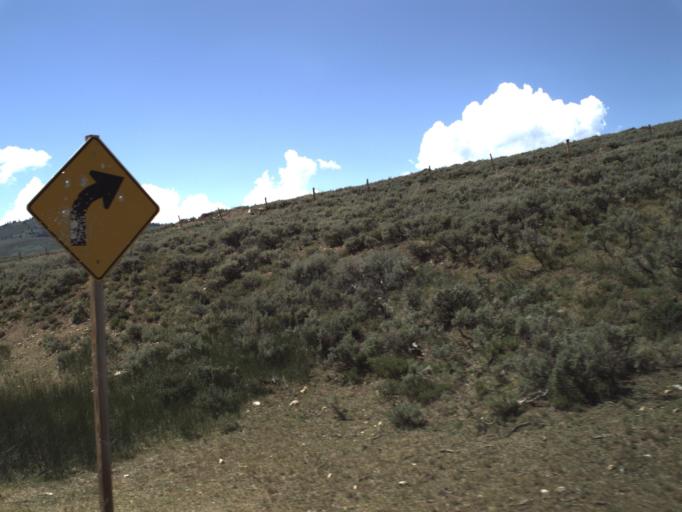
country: US
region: Utah
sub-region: Rich County
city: Randolph
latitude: 41.4838
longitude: -111.4117
